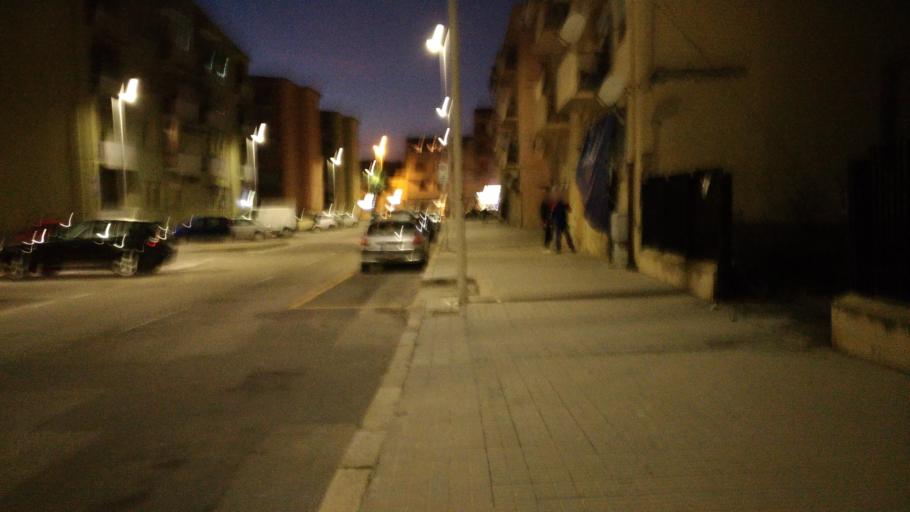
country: IT
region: Sardinia
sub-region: Provincia di Cagliari
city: Su Planu
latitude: 39.2396
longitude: 9.1035
